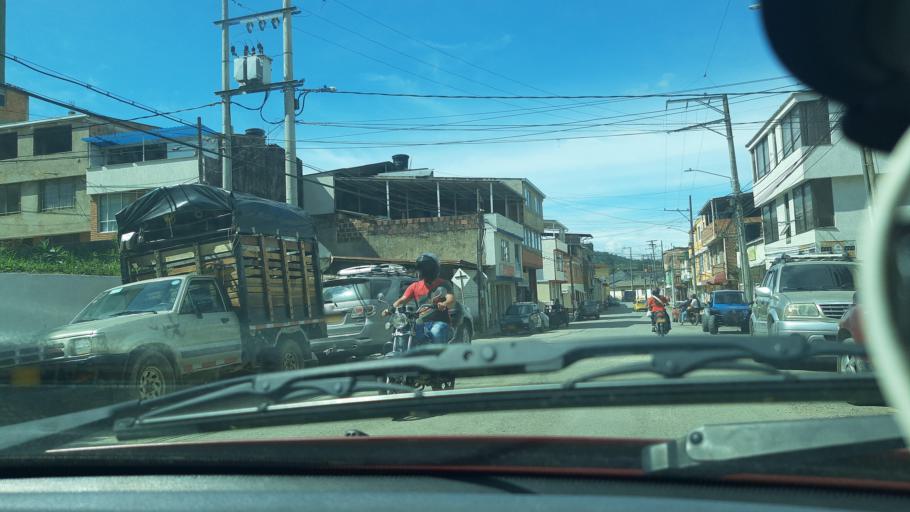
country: CO
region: Boyaca
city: Moniquira
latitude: 5.8745
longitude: -73.5740
